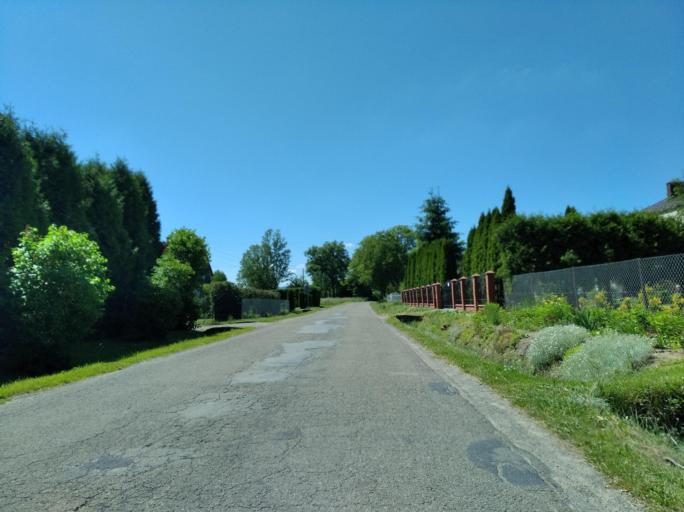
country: PL
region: Subcarpathian Voivodeship
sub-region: Powiat jasielski
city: Nowy Zmigrod
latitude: 49.6320
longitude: 21.5903
